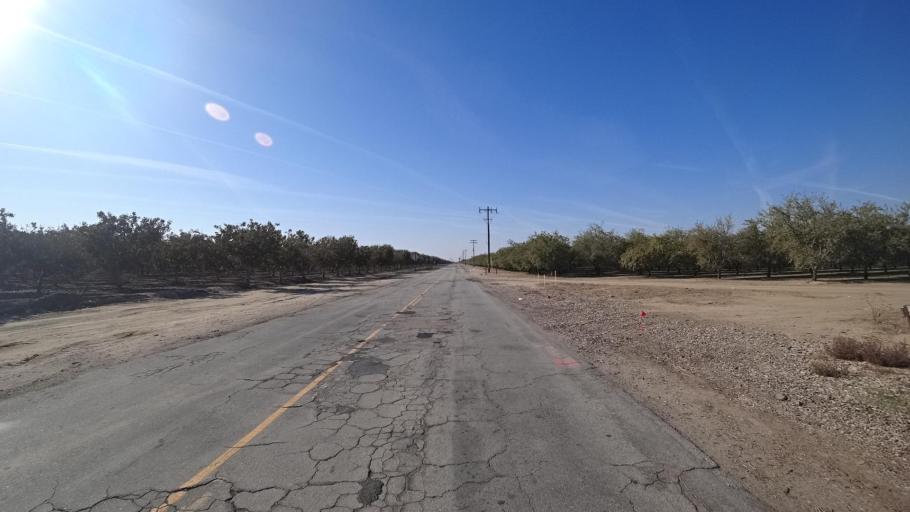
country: US
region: California
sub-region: Kern County
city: Wasco
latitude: 35.6526
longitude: -119.3323
